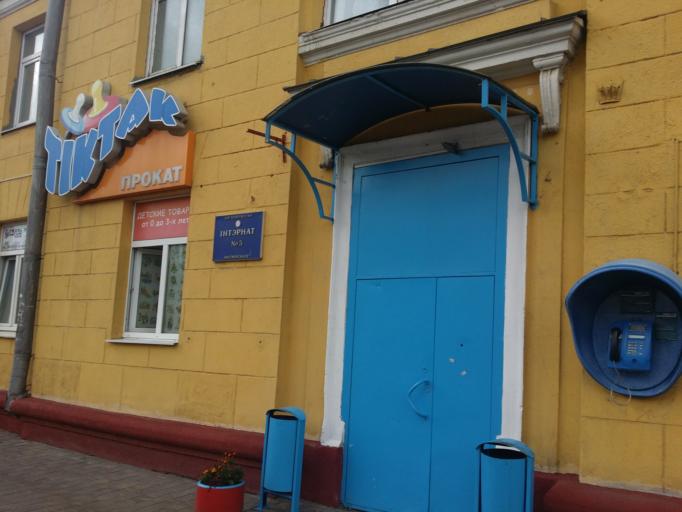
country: BY
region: Minsk
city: Minsk
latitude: 53.9161
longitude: 27.5722
